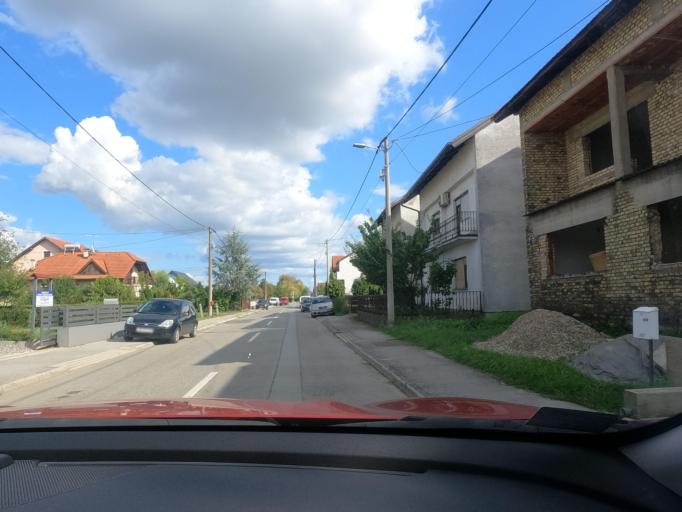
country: HR
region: Sisacko-Moslavacka
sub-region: Grad Sisak
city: Sisak
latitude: 45.5005
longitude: 16.3589
